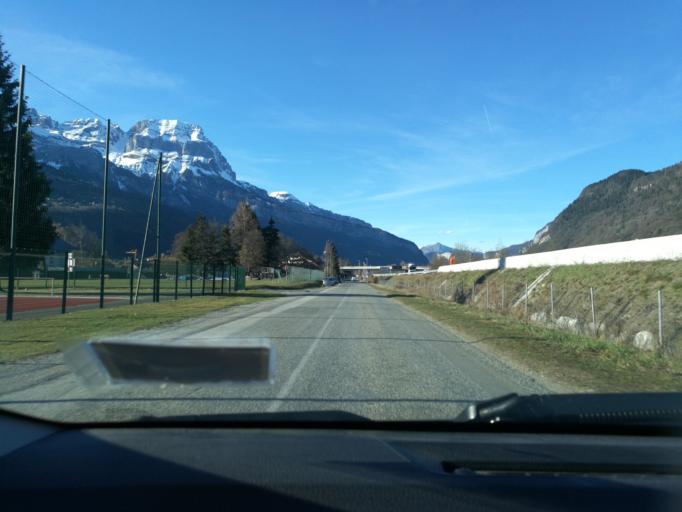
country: FR
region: Rhone-Alpes
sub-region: Departement de la Haute-Savoie
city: Sallanches
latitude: 45.9351
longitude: 6.6442
